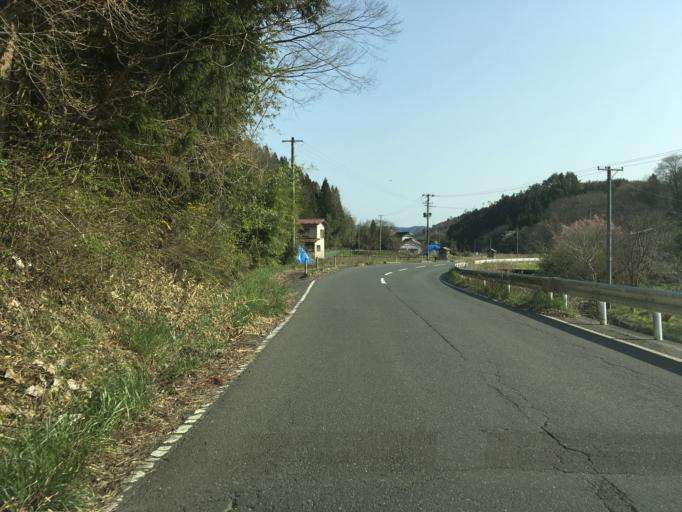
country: JP
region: Iwate
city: Ichinoseki
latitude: 38.8022
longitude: 141.3177
